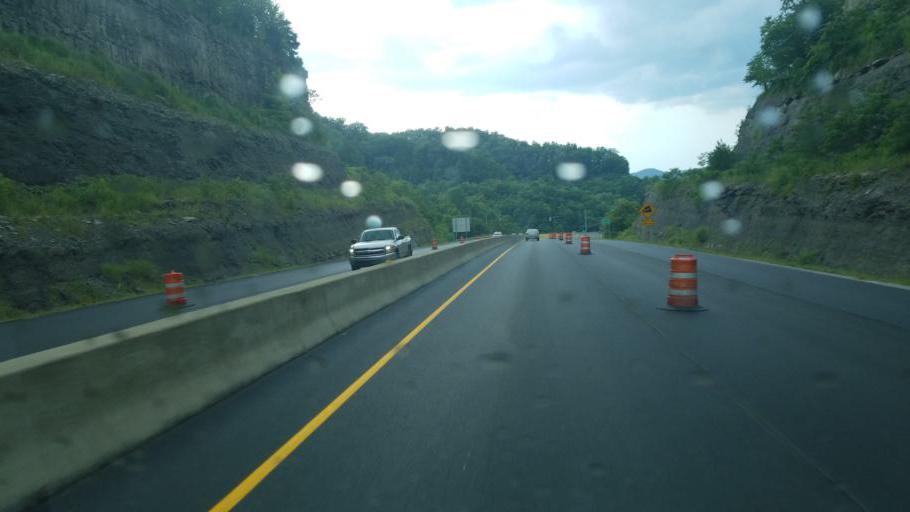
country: US
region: Kentucky
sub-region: Pike County
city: Pikeville
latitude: 37.5132
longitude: -82.4949
